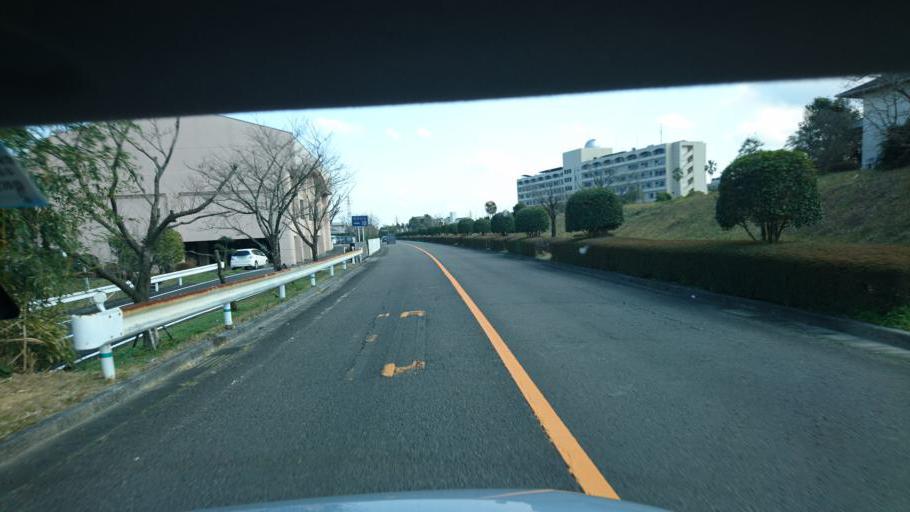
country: JP
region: Miyazaki
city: Miyazaki-shi
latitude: 31.8327
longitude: 131.4116
